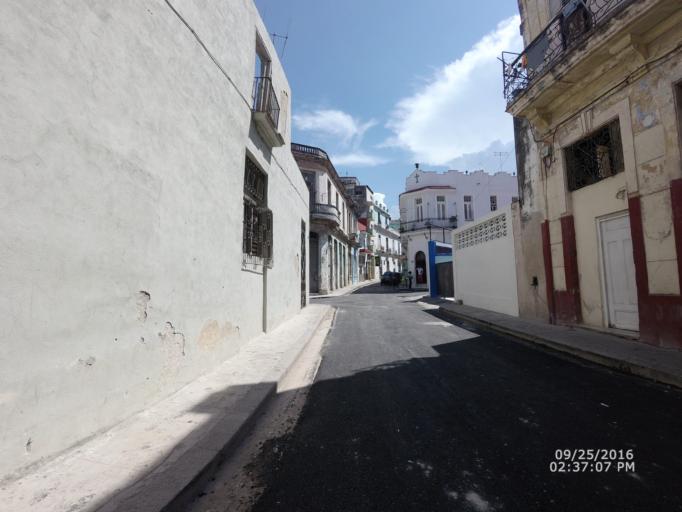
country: CU
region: La Habana
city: Centro Habana
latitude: 23.1429
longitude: -82.3552
